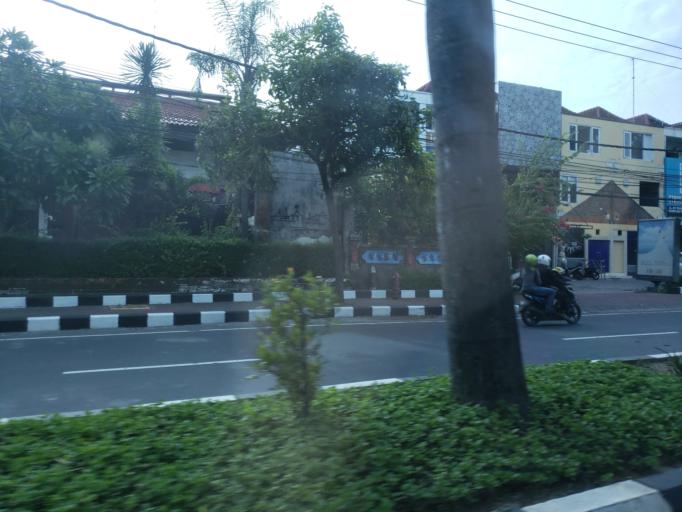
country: ID
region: Bali
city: Jabajero
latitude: -8.7347
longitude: 115.1792
